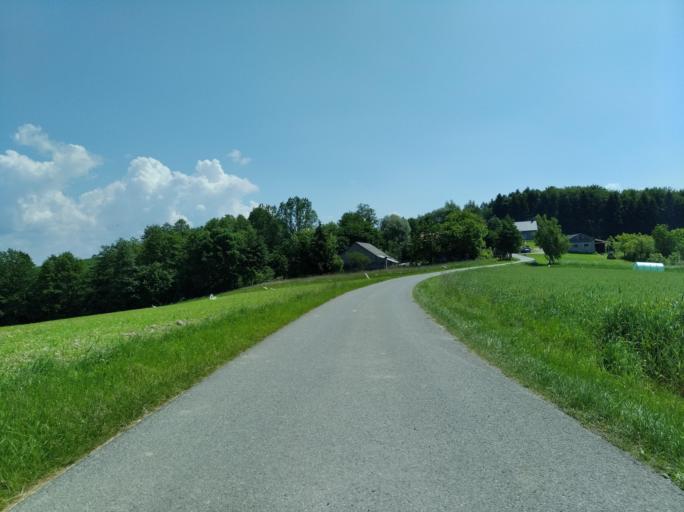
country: PL
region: Subcarpathian Voivodeship
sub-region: Powiat ropczycko-sedziszowski
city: Wielopole Skrzynskie
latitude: 49.9843
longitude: 21.6095
